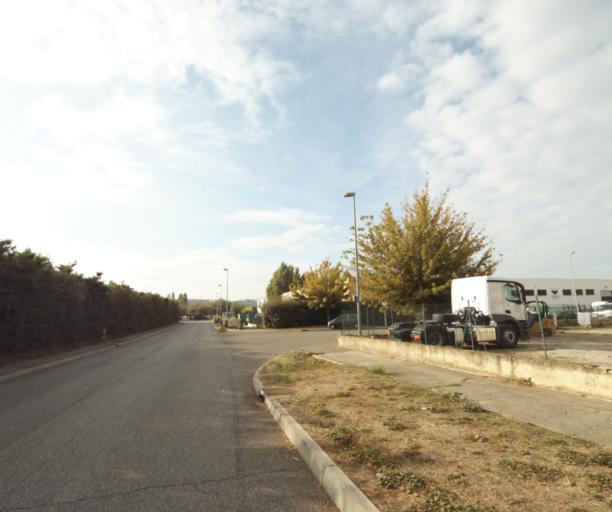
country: FR
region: Provence-Alpes-Cote d'Azur
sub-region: Departement des Bouches-du-Rhone
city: Saint-Victoret
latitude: 43.4198
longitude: 5.2605
